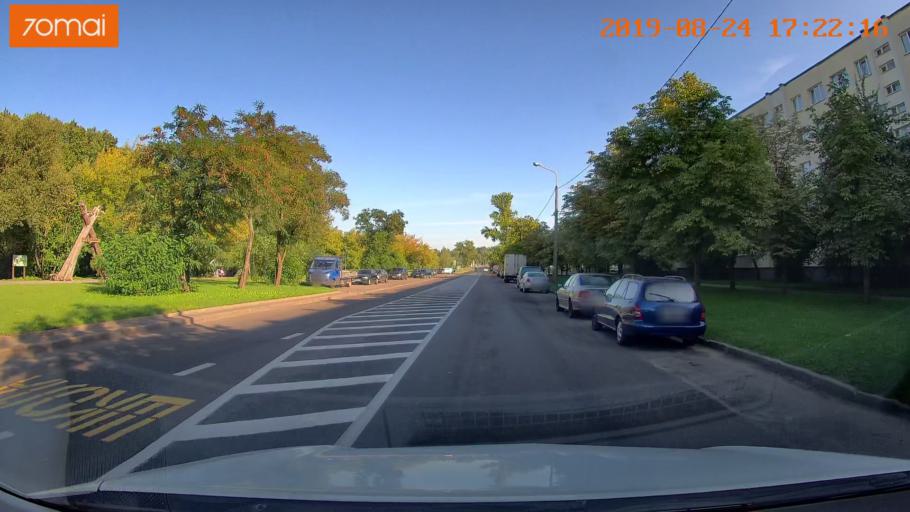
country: BY
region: Minsk
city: Hatava
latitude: 53.8466
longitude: 27.6426
